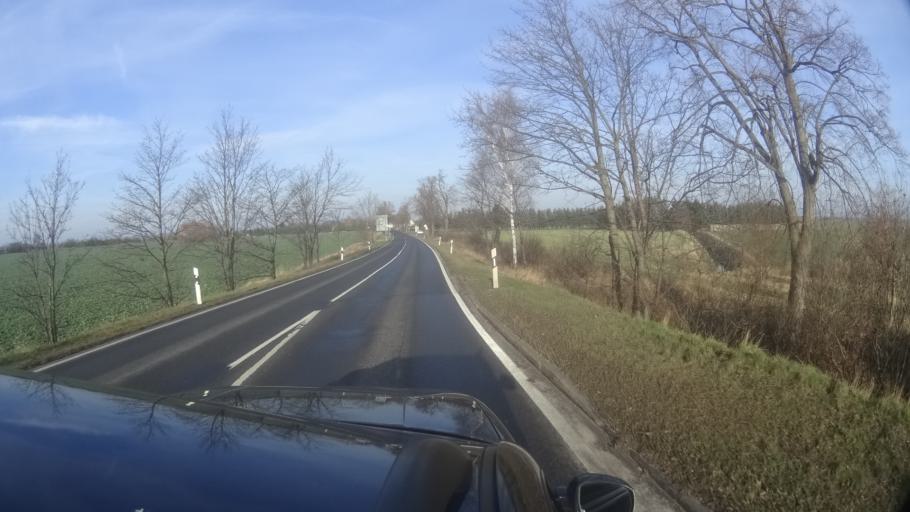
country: DE
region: Brandenburg
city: Velten
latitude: 52.7095
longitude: 13.1041
